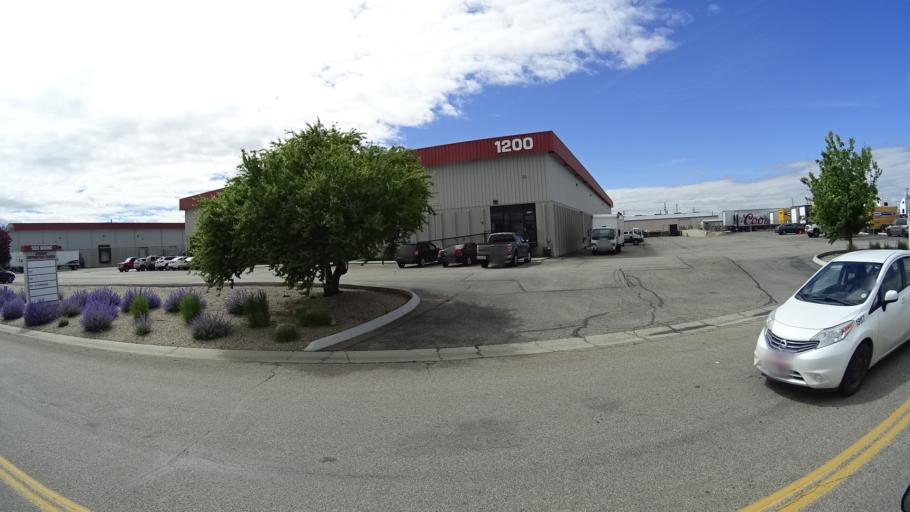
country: US
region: Idaho
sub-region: Ada County
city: Boise
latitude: 43.5625
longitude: -116.1971
